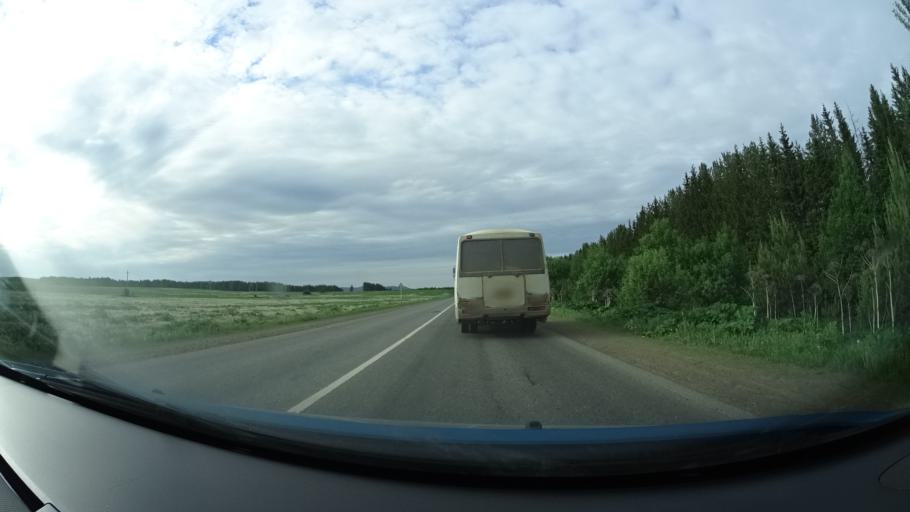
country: RU
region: Perm
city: Osa
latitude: 57.2669
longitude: 55.5730
